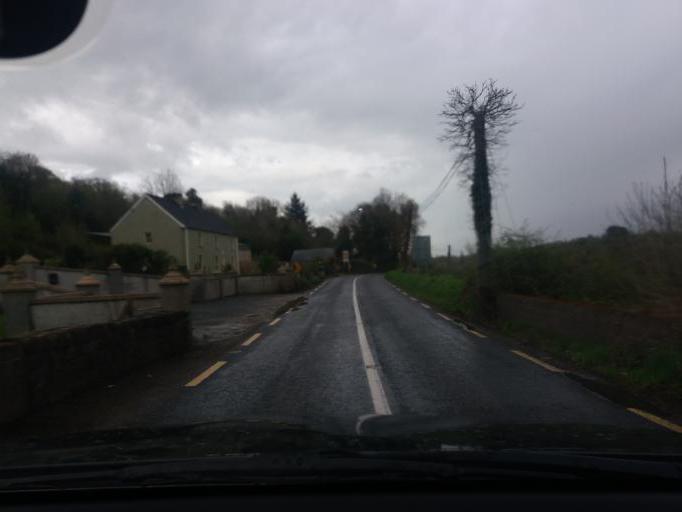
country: IE
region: Ulster
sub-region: An Cabhan
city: Ballyconnell
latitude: 54.1325
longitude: -7.6898
